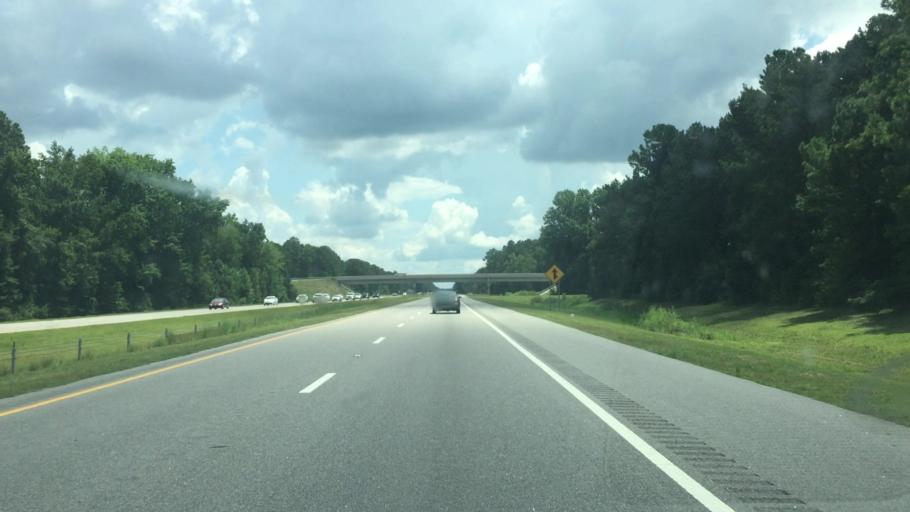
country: US
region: North Carolina
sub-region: Columbus County
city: Chadbourn
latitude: 34.3978
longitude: -78.9042
